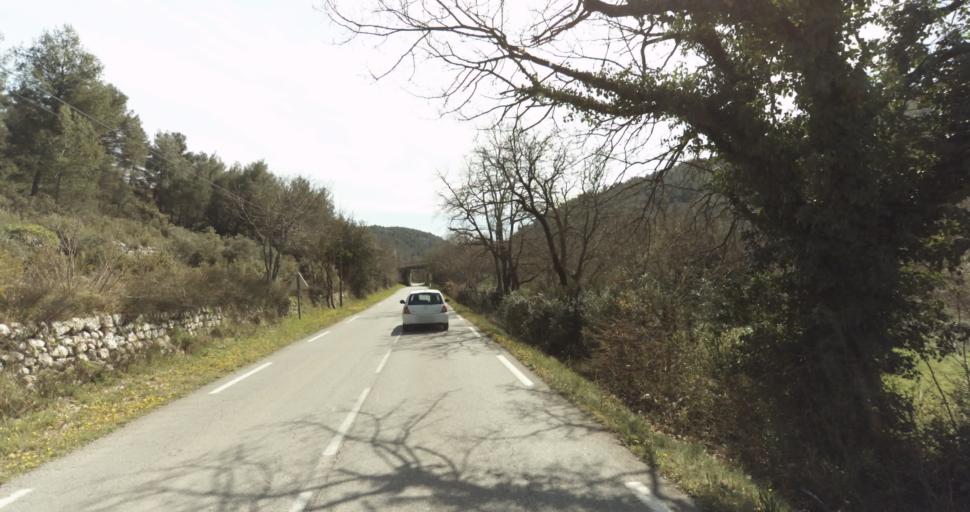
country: FR
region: Provence-Alpes-Cote d'Azur
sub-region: Departement des Bouches-du-Rhone
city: Ventabren
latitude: 43.5177
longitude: 5.3036
